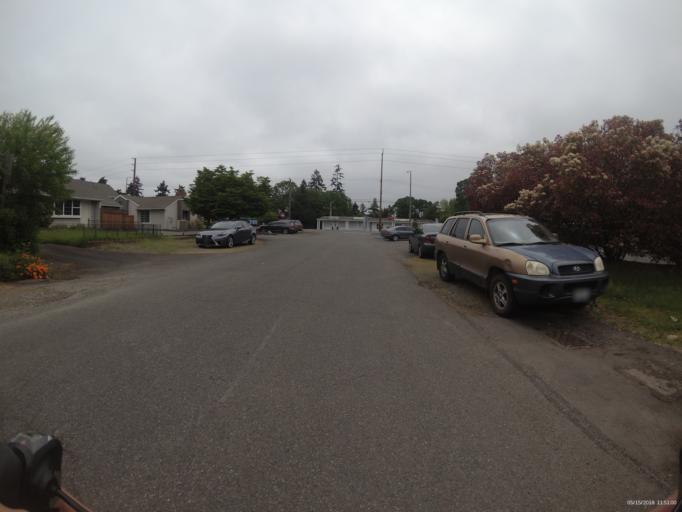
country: US
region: Washington
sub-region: Pierce County
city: Lakewood
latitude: 47.1743
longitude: -122.5206
